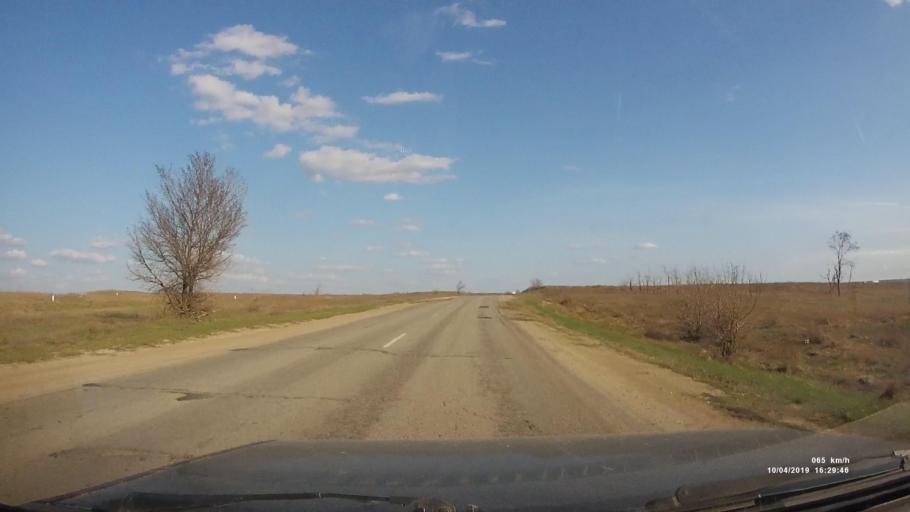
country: RU
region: Rostov
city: Staraya Stanitsa
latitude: 48.2666
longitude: 40.3588
